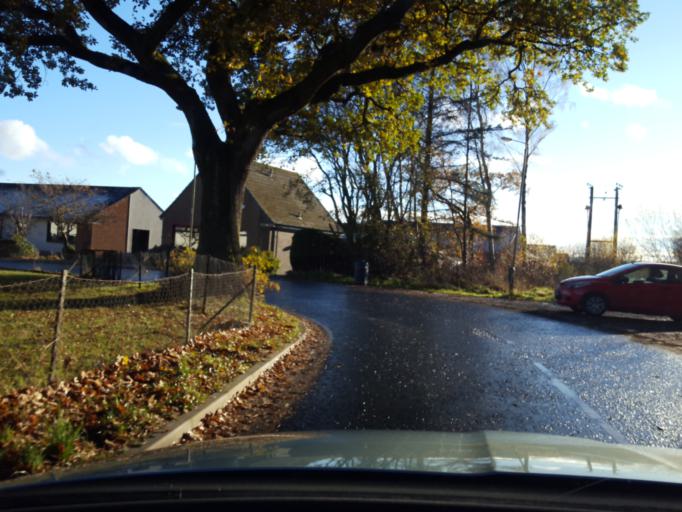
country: GB
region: Scotland
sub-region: Perth and Kinross
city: Scone
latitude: 56.4241
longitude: -3.4151
